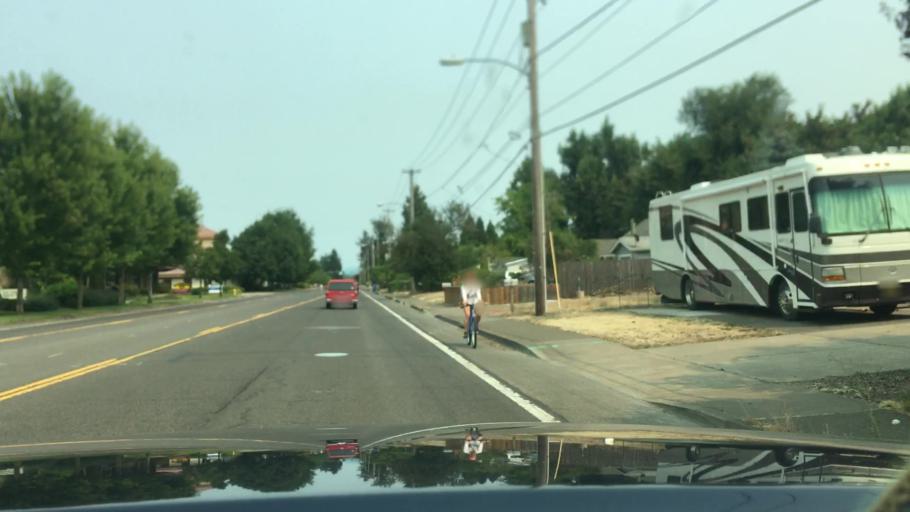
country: US
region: Oregon
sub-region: Lane County
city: Eugene
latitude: 44.0845
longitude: -123.1658
